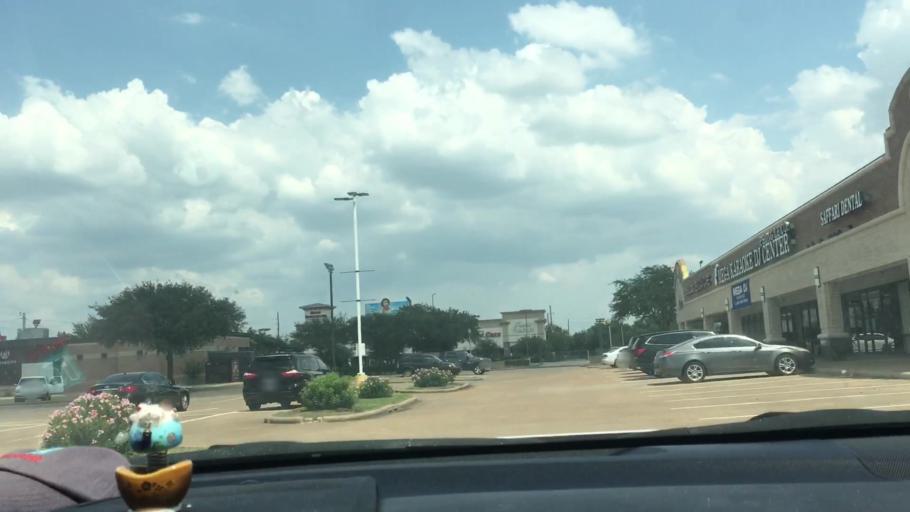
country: US
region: Texas
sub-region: Fort Bend County
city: Mission Bend
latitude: 29.7349
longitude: -95.6379
